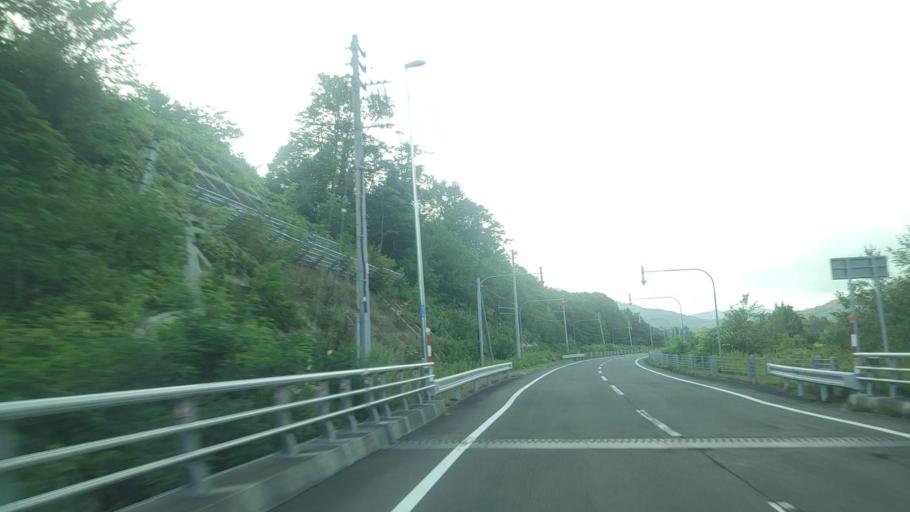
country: JP
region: Hokkaido
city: Bibai
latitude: 43.0740
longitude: 142.1026
